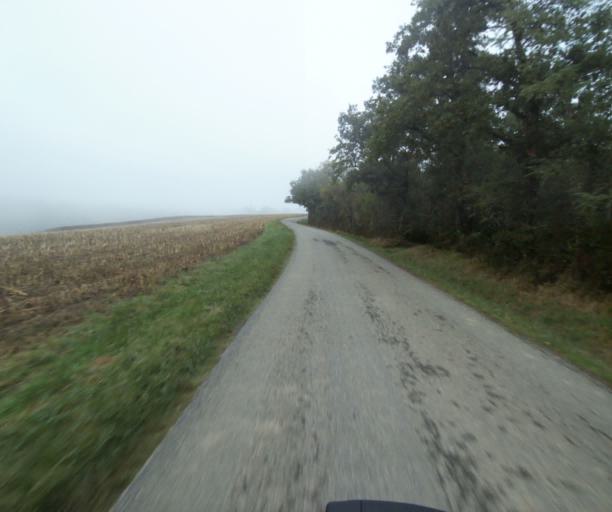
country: FR
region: Midi-Pyrenees
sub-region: Departement du Tarn-et-Garonne
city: Saint-Nauphary
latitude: 43.9440
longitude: 1.4110
